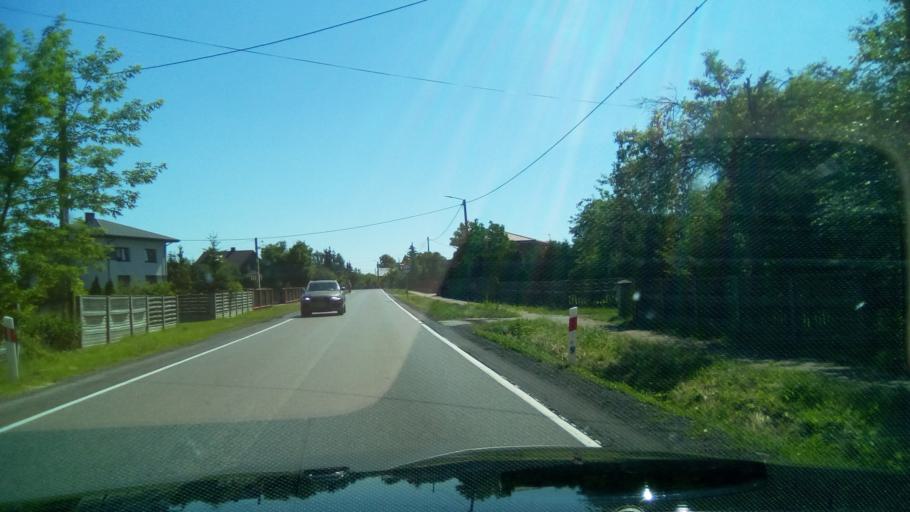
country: PL
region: Lodz Voivodeship
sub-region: Powiat opoczynski
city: Poswietne
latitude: 51.5245
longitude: 20.3449
